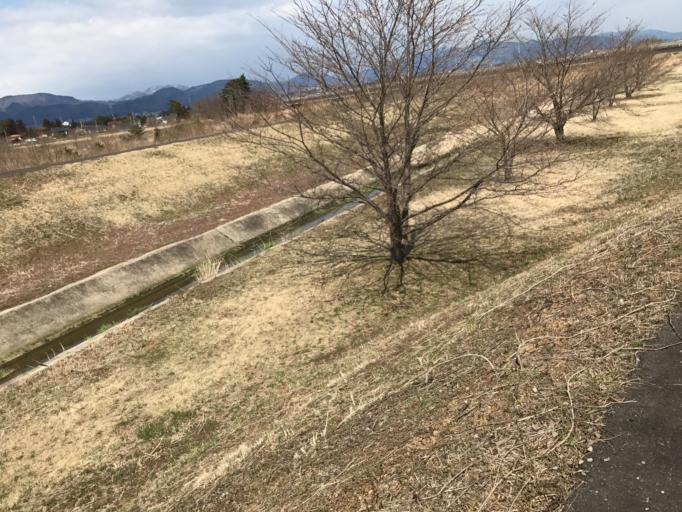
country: JP
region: Fukushima
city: Fukushima-shi
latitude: 37.7442
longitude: 140.4027
